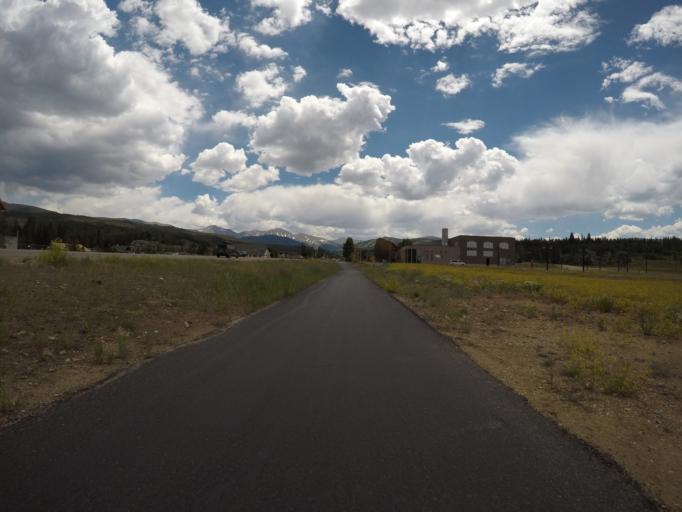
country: US
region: Colorado
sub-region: Grand County
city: Fraser
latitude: 39.9290
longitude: -105.7894
